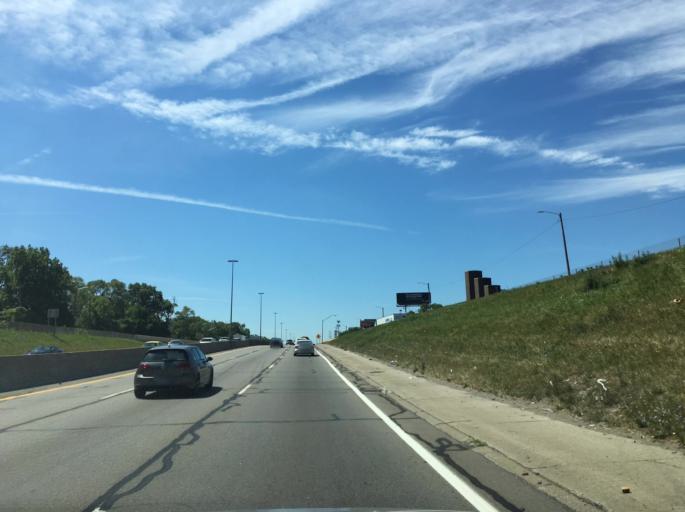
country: US
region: Michigan
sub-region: Wayne County
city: Dearborn
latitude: 42.3720
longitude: -83.2168
